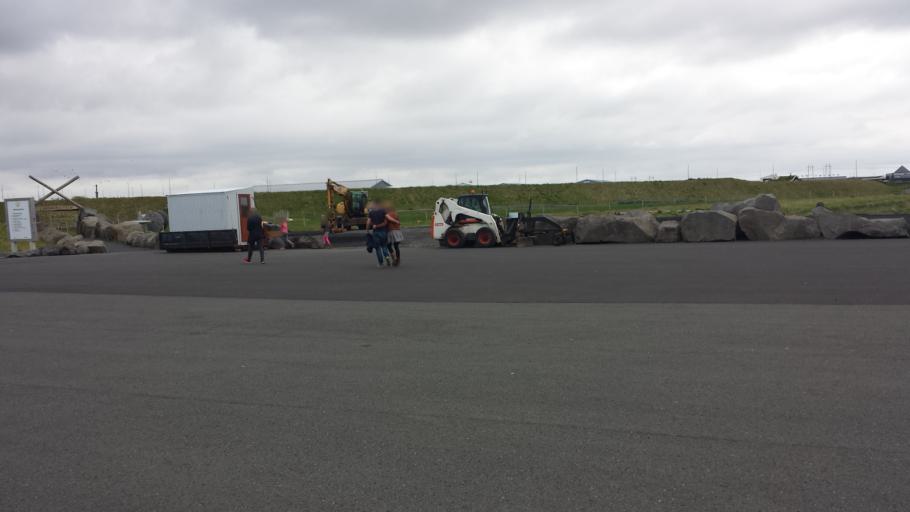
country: IS
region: Southern Peninsula
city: Reykjanesbaer
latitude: 63.9757
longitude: -22.5285
